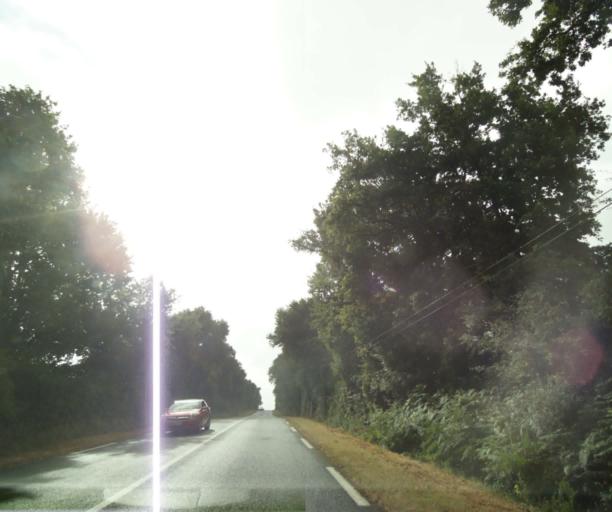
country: FR
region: Pays de la Loire
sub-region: Departement de la Vendee
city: Avrille
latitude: 46.4633
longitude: -1.4607
